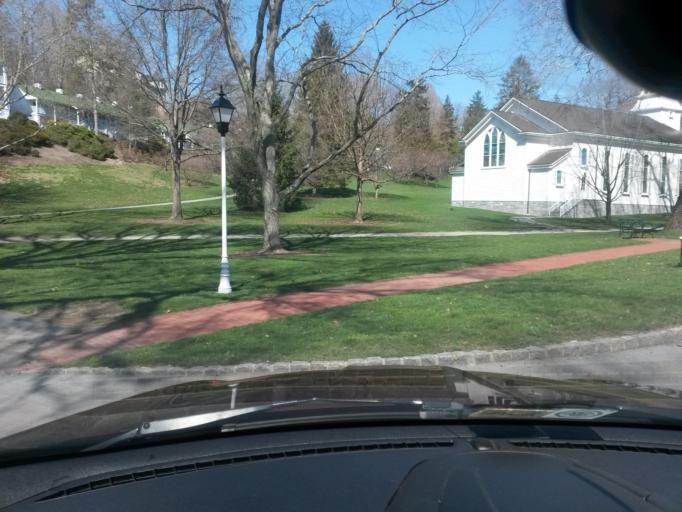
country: US
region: West Virginia
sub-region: Greenbrier County
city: White Sulphur Springs
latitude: 37.7875
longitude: -80.3115
